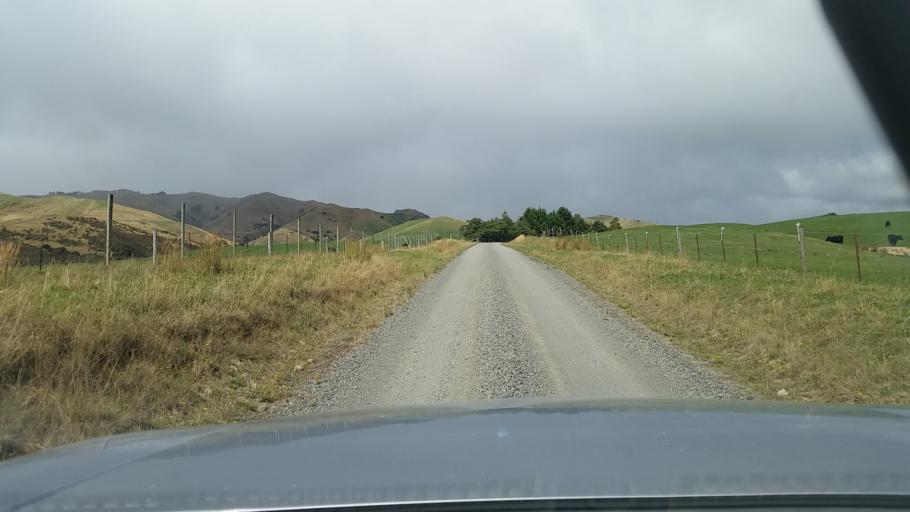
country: NZ
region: Marlborough
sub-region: Marlborough District
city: Blenheim
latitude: -41.7483
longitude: 173.8955
